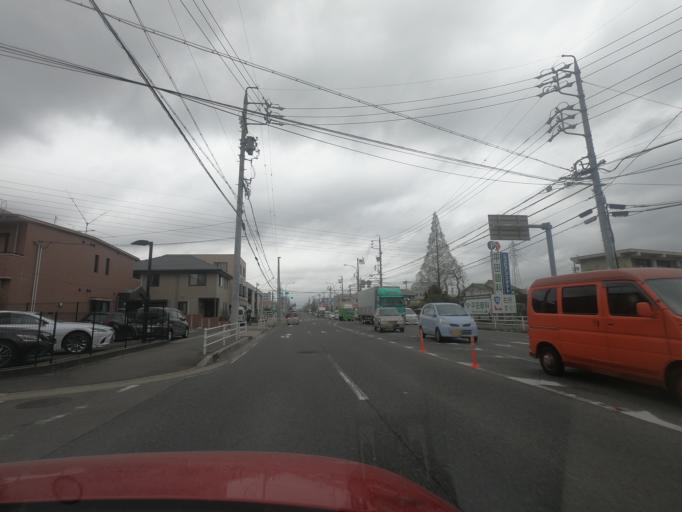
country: JP
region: Aichi
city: Kasugai
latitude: 35.2502
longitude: 136.9722
